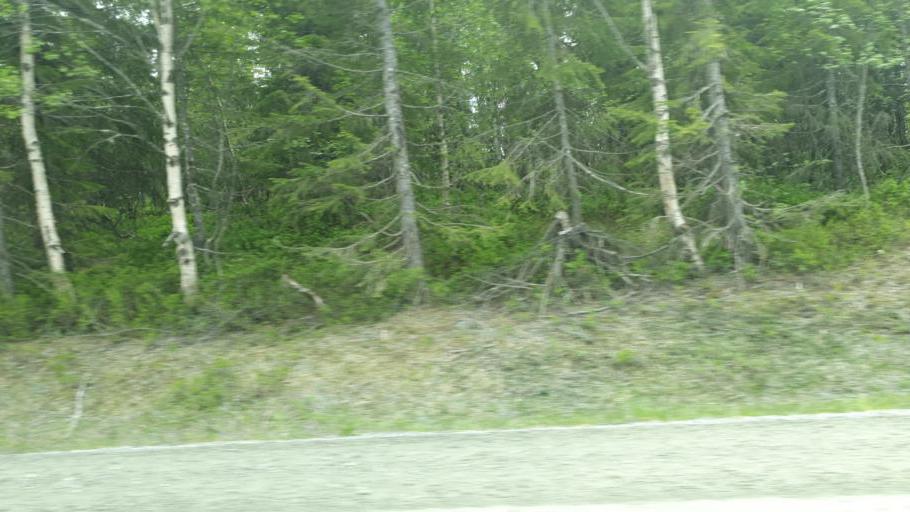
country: NO
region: Nord-Trondelag
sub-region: Leksvik
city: Leksvik
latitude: 63.6833
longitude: 10.3737
